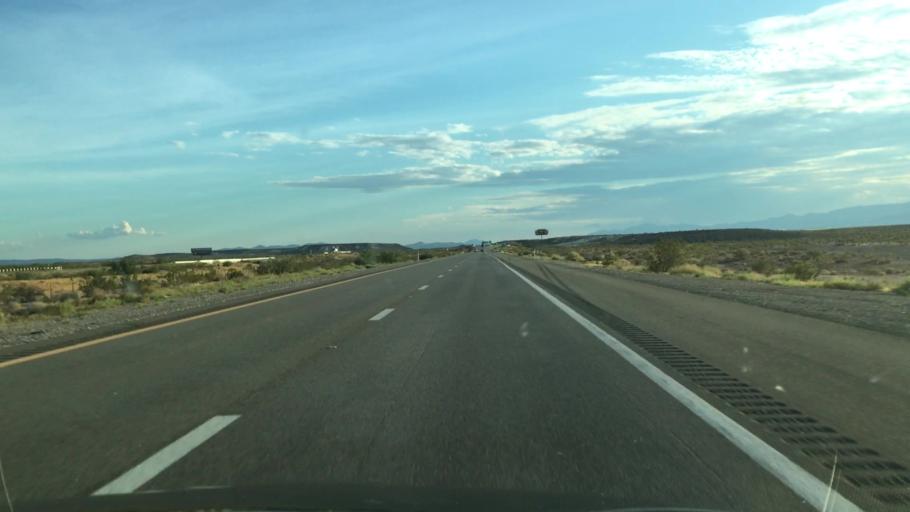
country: US
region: Nevada
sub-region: Clark County
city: Moapa Town
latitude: 36.5588
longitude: -114.6887
